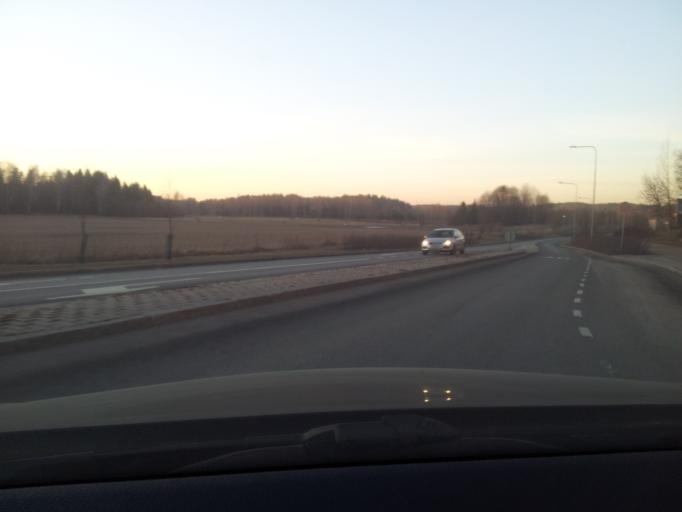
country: FI
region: Uusimaa
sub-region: Helsinki
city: Kilo
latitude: 60.2143
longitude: 24.8004
